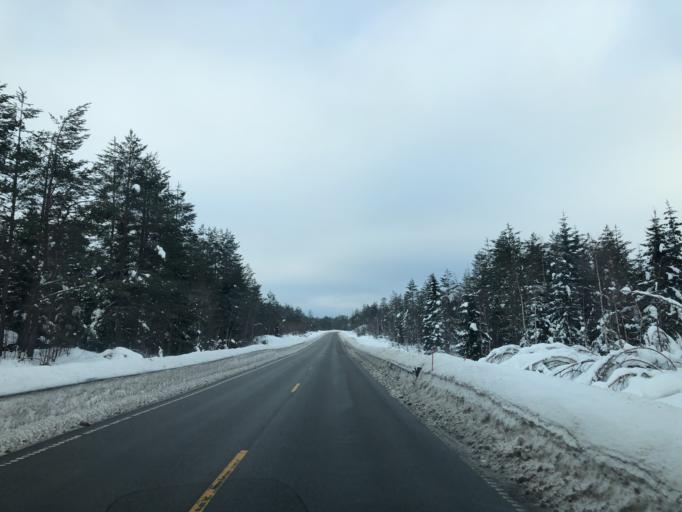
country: NO
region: Hedmark
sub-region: Trysil
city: Innbygda
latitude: 61.1916
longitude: 12.2019
